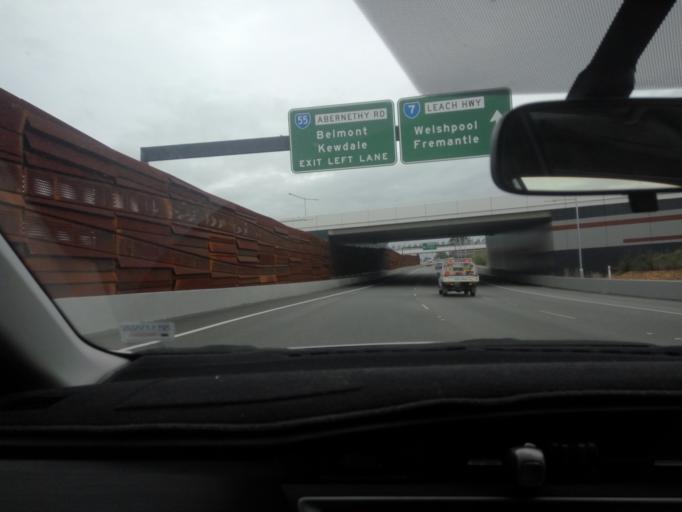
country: AU
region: Western Australia
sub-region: Belmont
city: Kewdale
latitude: -31.9666
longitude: 115.9557
